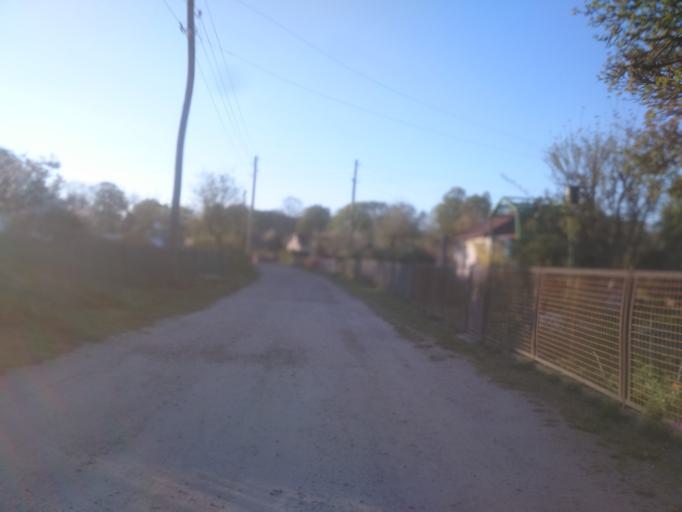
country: DE
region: Berlin
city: Stadtrandsiedlung Malchow
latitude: 52.5765
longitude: 13.4689
